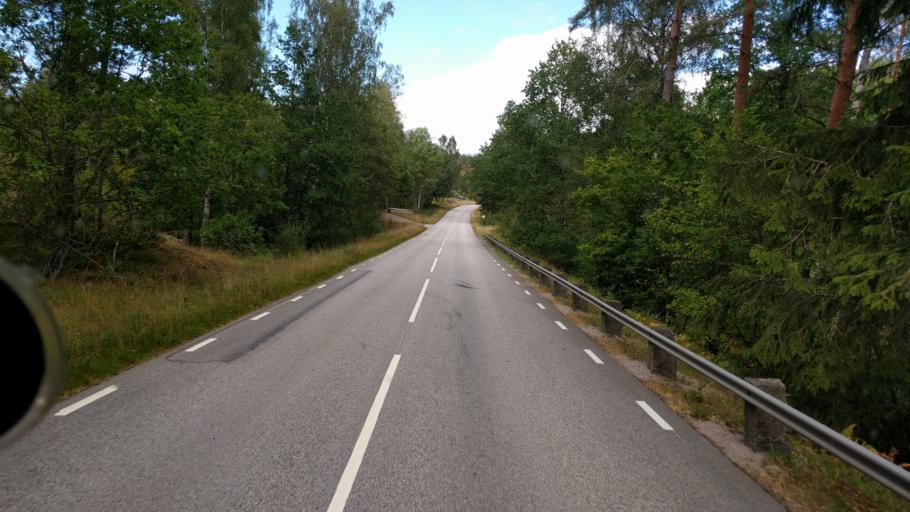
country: SE
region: Kalmar
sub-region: Vasterviks Kommun
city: Ankarsrum
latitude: 57.7555
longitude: 16.1235
